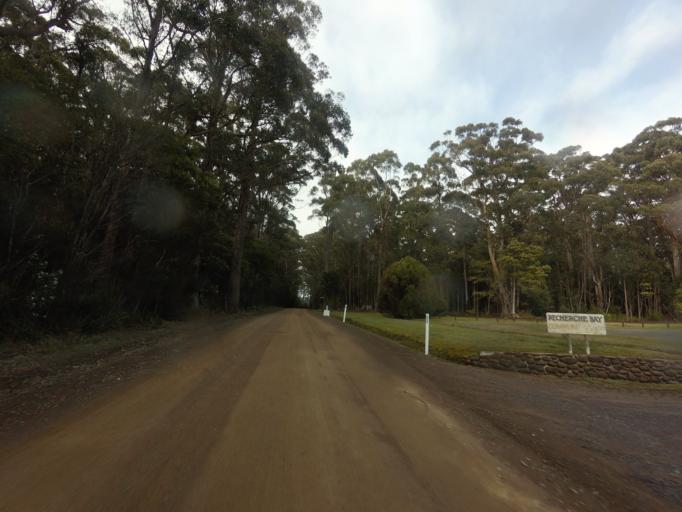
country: AU
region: Tasmania
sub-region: Huon Valley
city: Geeveston
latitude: -43.5396
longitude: 146.8920
